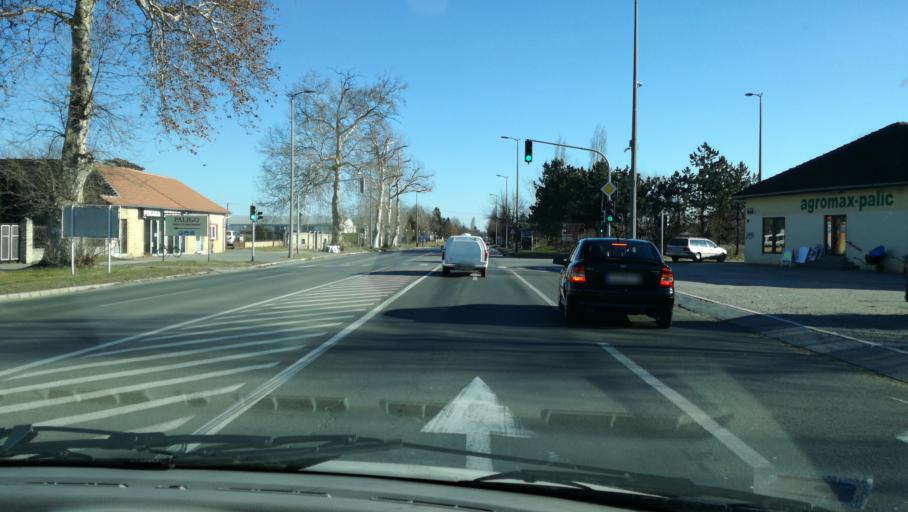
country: RS
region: Autonomna Pokrajina Vojvodina
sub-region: Severnobacki Okrug
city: Subotica
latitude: 46.1020
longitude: 19.7629
